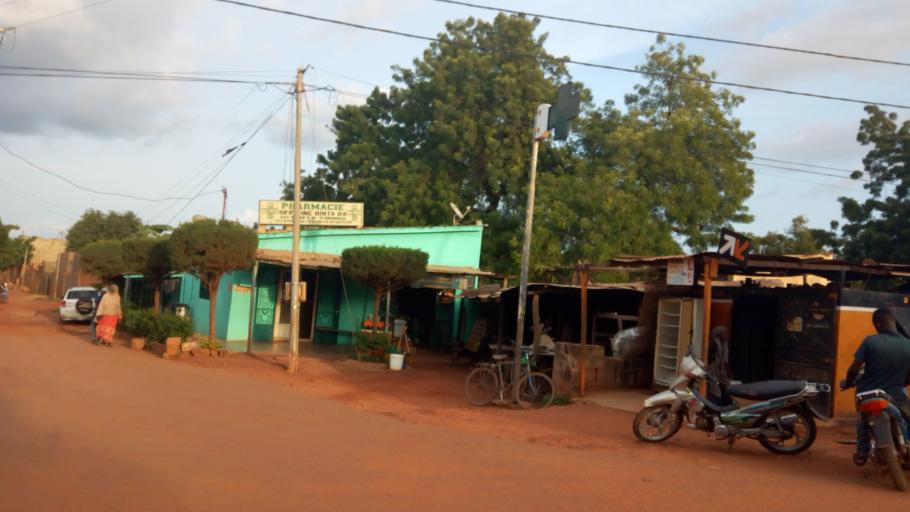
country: ML
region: Sikasso
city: Koutiala
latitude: 12.3795
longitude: -5.4720
